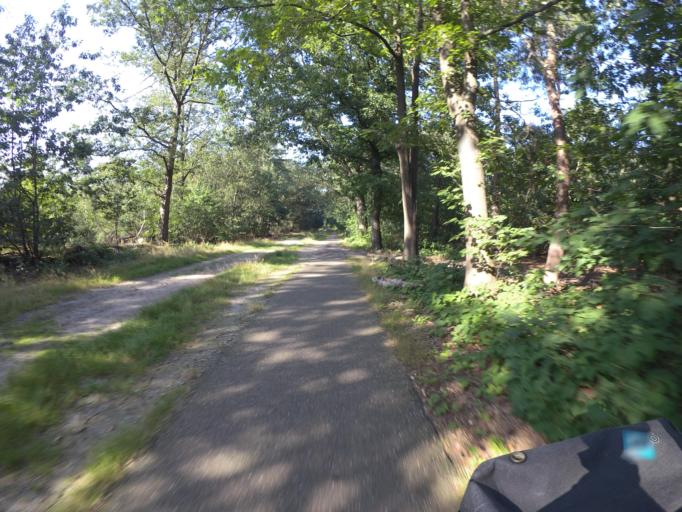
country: NL
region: North Brabant
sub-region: Gemeente Landerd
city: Schaijk
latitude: 51.7206
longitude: 5.6295
